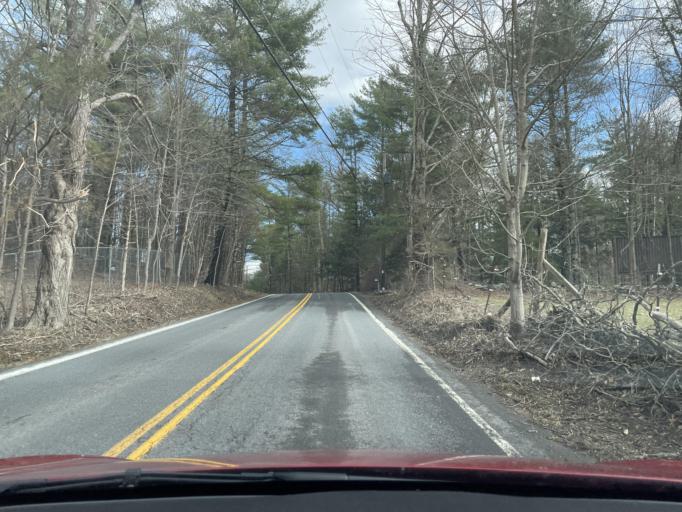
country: US
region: New York
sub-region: Ulster County
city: Zena
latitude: 42.0461
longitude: -74.0421
